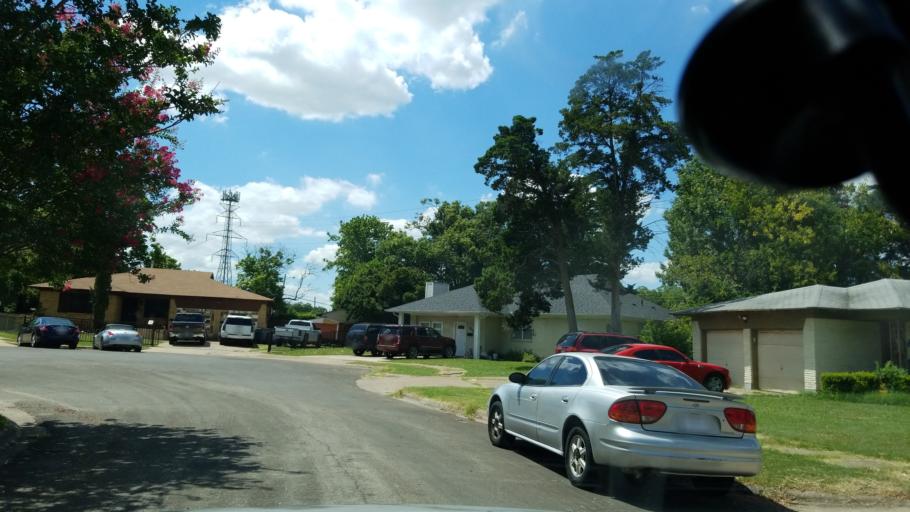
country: US
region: Texas
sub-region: Dallas County
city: Cockrell Hill
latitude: 32.6986
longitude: -96.8693
